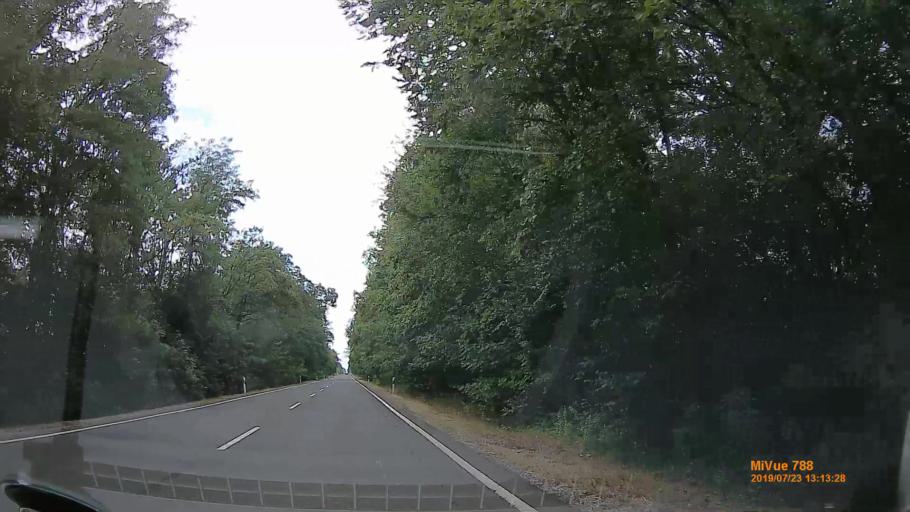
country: HU
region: Hajdu-Bihar
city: Gorbehaza
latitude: 47.9247
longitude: 21.2303
